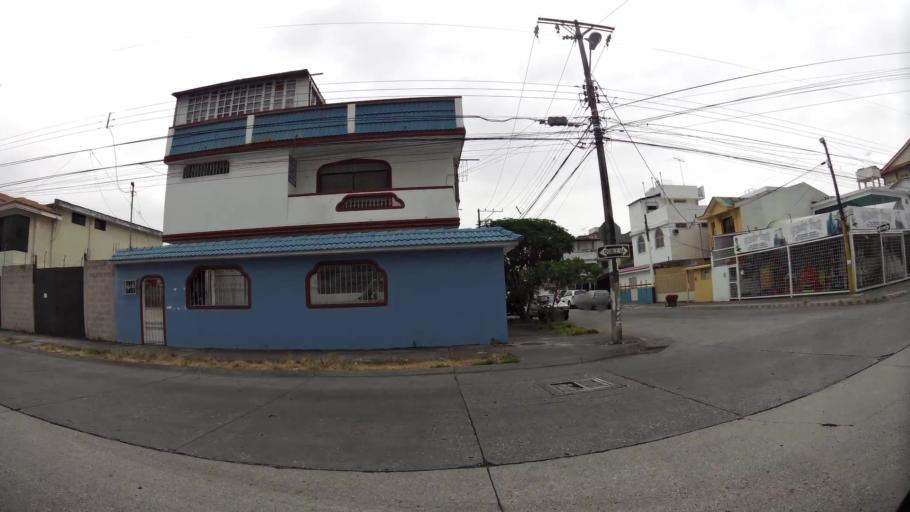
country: EC
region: Guayas
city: Eloy Alfaro
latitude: -2.1484
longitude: -79.8898
